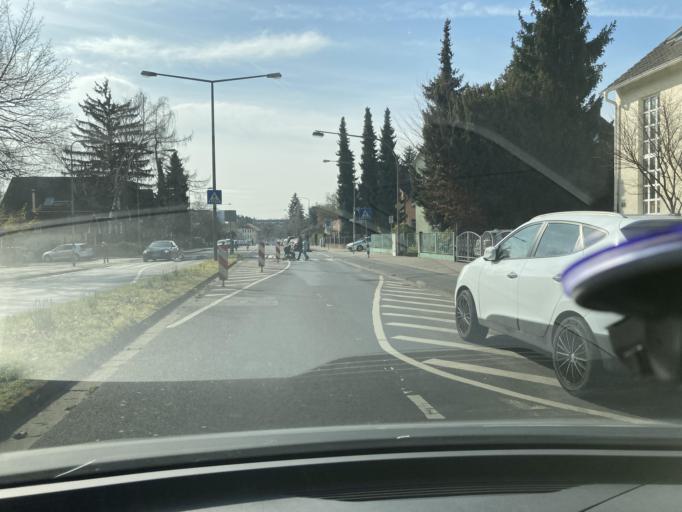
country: DE
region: Hesse
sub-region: Regierungsbezirk Darmstadt
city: Steinbach am Taunus
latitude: 50.1550
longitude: 8.6283
